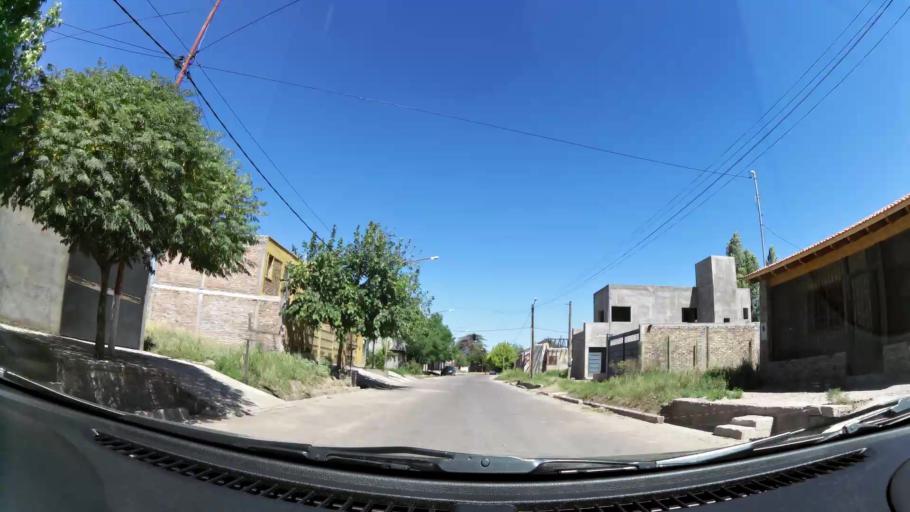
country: AR
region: Mendoza
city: Las Heras
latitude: -32.8548
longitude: -68.8479
